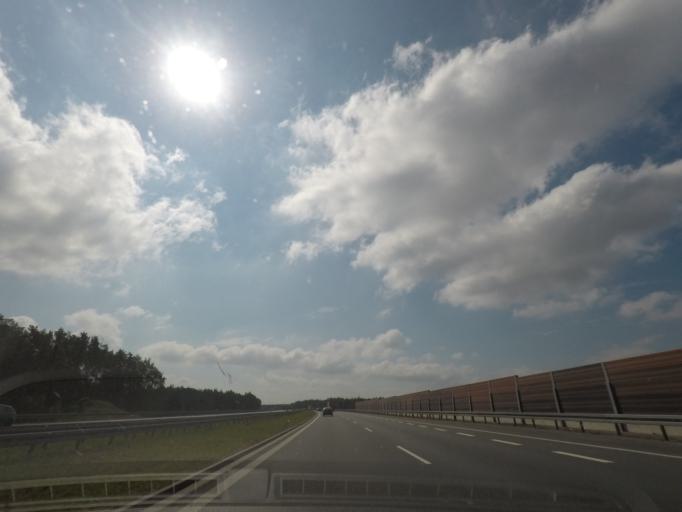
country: PL
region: Kujawsko-Pomorskie
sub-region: Powiat aleksandrowski
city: Aleksandrow Kujawski
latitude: 52.8956
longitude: 18.7256
